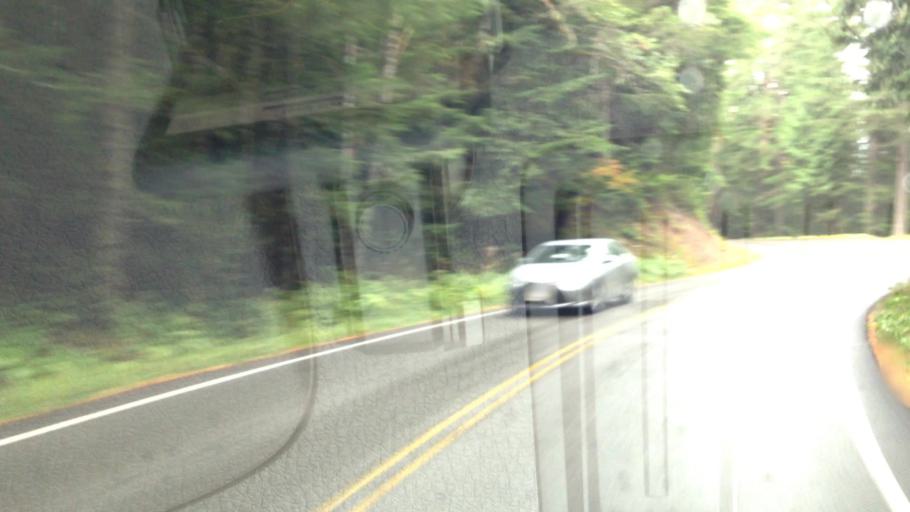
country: US
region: Washington
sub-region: Pierce County
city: Eatonville
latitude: 46.7362
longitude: -121.8302
